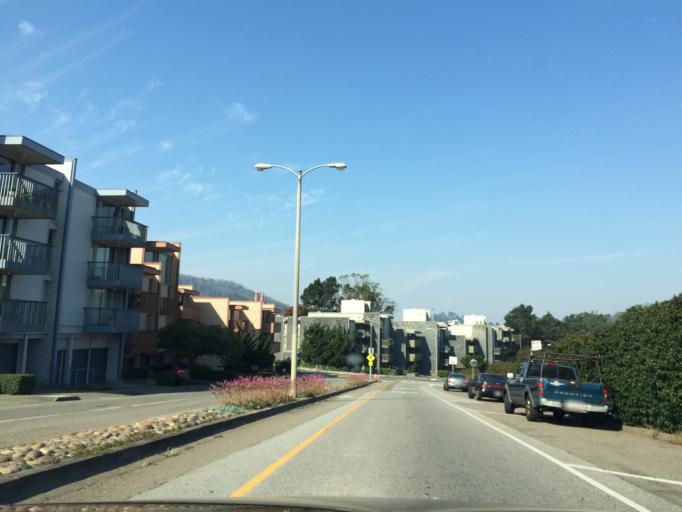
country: US
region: California
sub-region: San Francisco County
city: San Francisco
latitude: 37.7469
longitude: -122.4424
